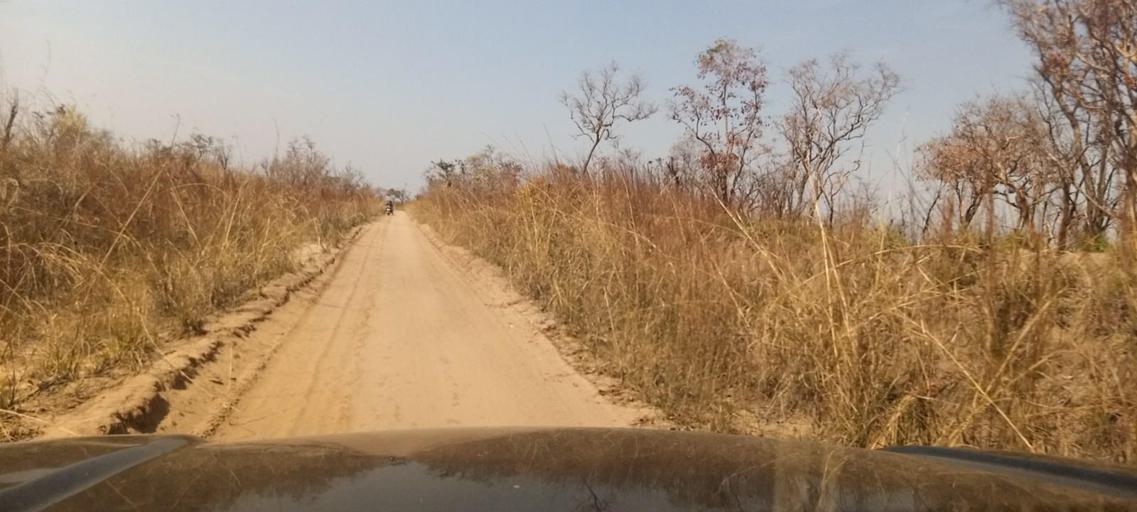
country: CD
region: Kasai-Oriental
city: Kabinda
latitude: -5.7925
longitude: 25.0432
